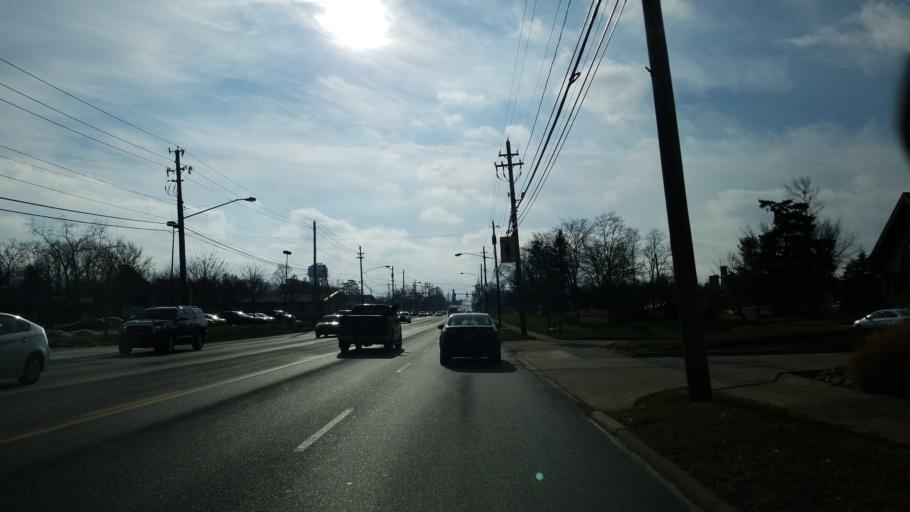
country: US
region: Ohio
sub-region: Cuyahoga County
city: Strongsville
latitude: 41.3226
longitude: -81.8365
